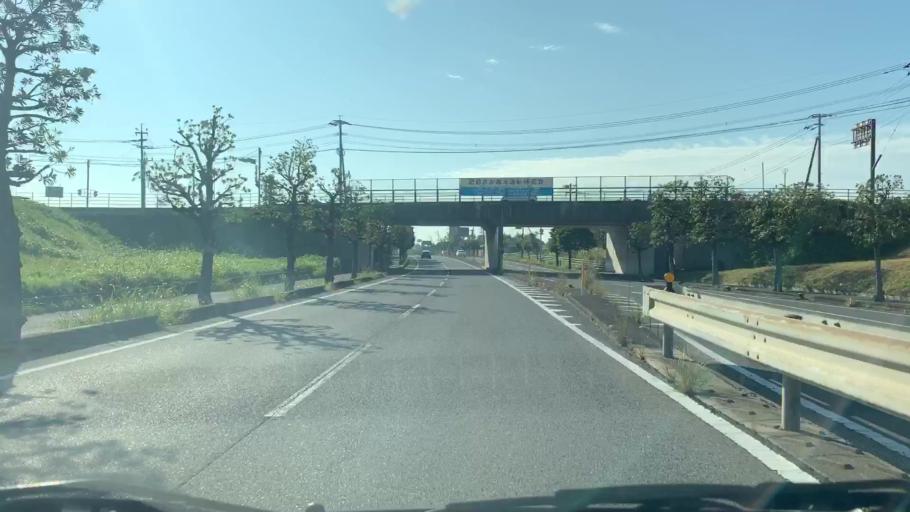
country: JP
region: Saga Prefecture
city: Saga-shi
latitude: 33.3099
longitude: 130.2765
